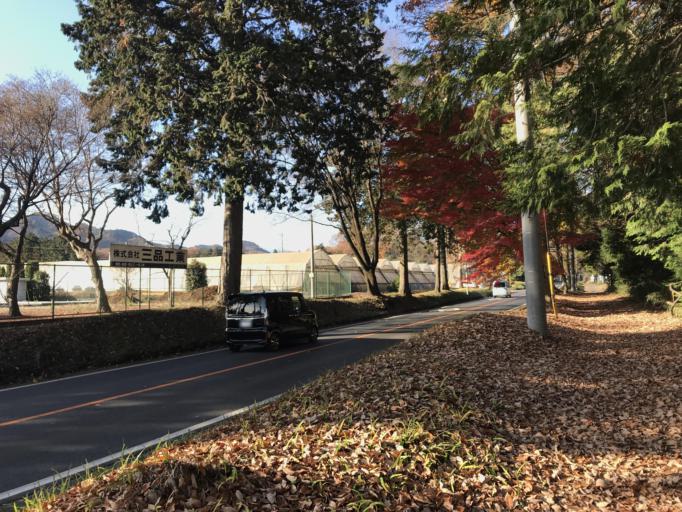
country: JP
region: Tochigi
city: Kanuma
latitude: 36.6119
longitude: 139.7393
